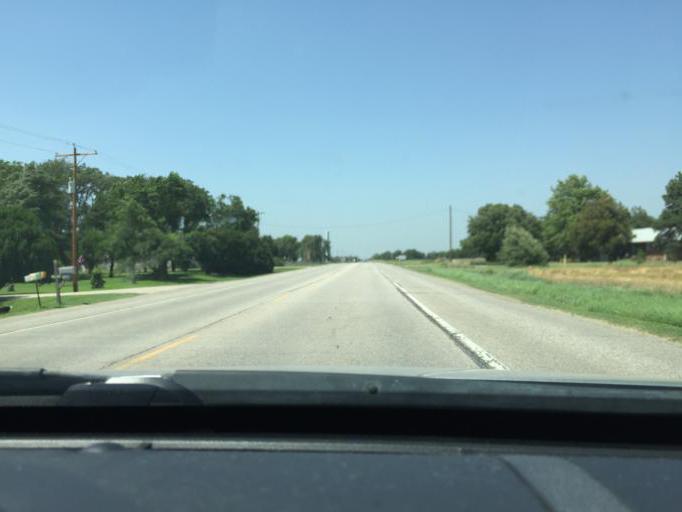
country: US
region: Kansas
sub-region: Reno County
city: Haven
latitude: 37.9475
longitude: -97.8668
